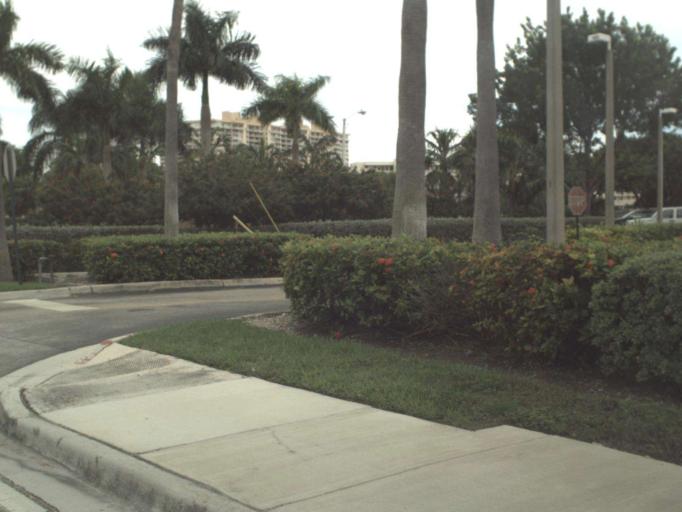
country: US
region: Florida
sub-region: Miami-Dade County
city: Ojus
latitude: 25.9393
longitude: -80.1493
